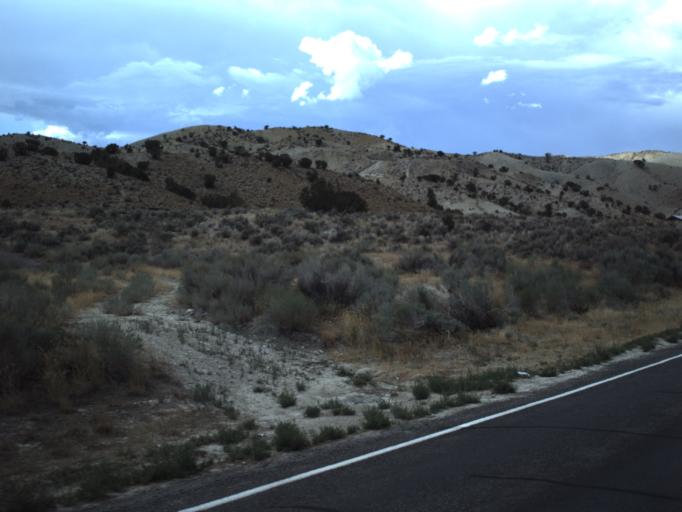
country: US
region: Utah
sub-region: Sanpete County
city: Centerfield
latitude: 39.1313
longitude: -111.7275
